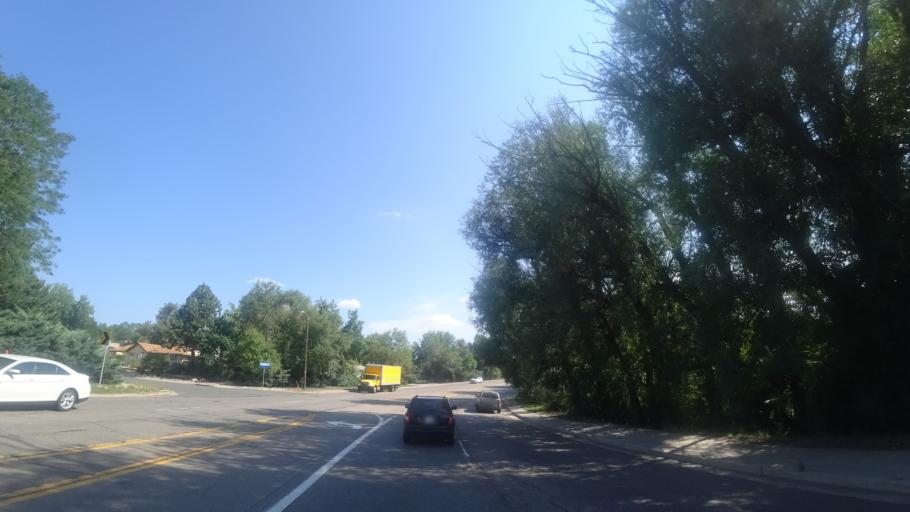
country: US
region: Colorado
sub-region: Arapahoe County
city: Southglenn
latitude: 39.5995
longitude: -104.9572
